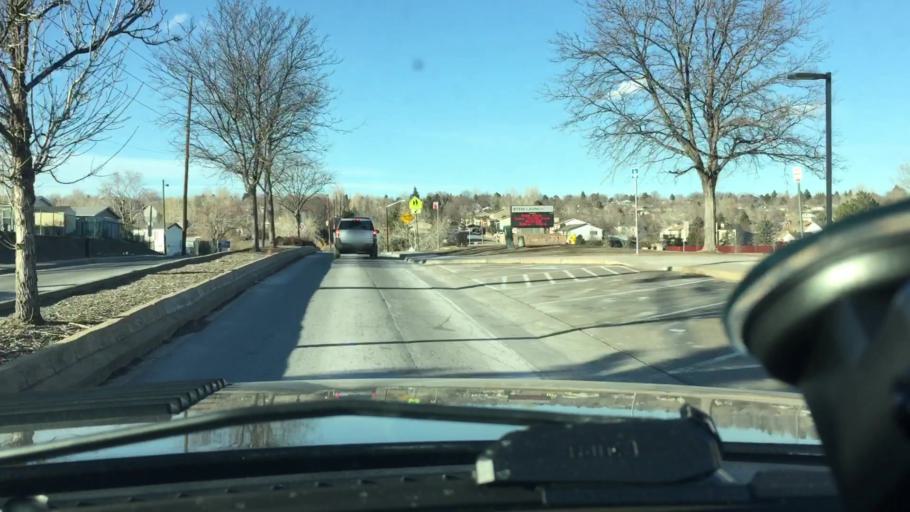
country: US
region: Colorado
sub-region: Adams County
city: Federal Heights
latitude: 39.8689
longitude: -105.0061
